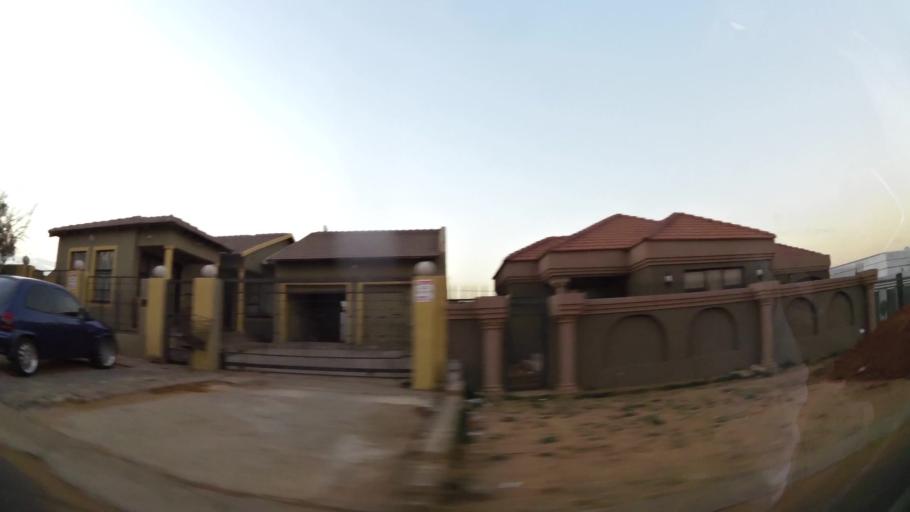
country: ZA
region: Gauteng
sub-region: West Rand District Municipality
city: Randfontein
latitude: -26.2111
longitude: 27.7112
